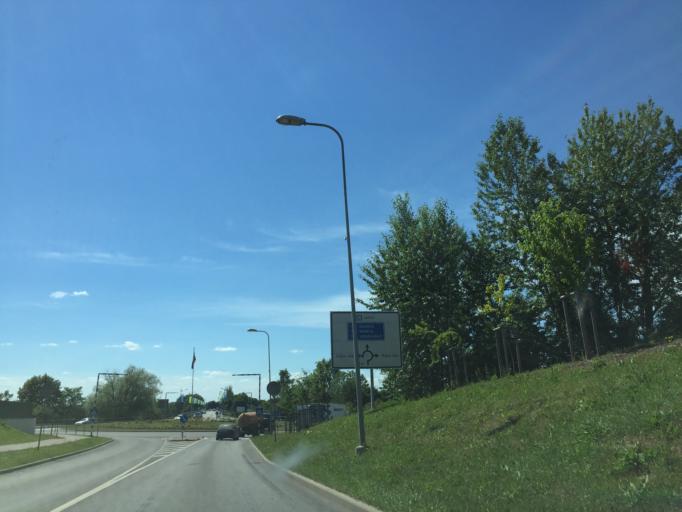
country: LV
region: Jekabpils Rajons
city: Jekabpils
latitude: 56.5026
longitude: 25.8785
